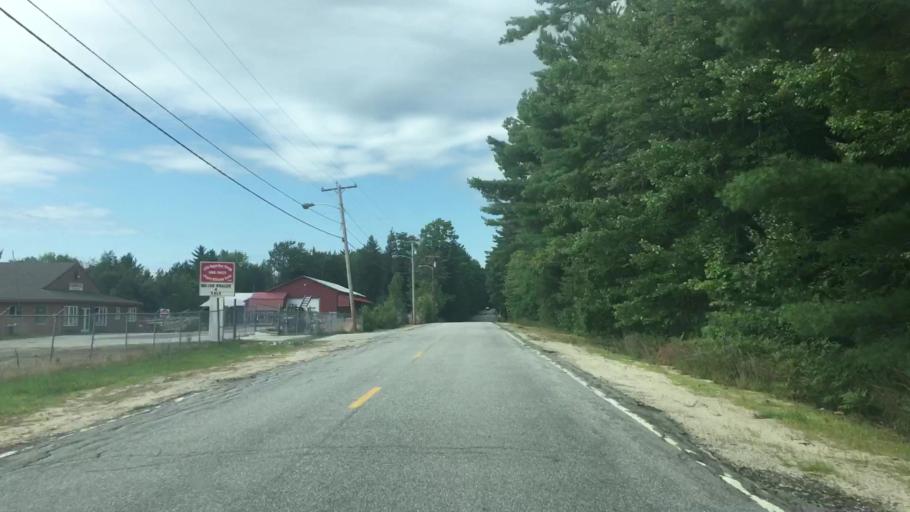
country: US
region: Maine
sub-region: Oxford County
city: Oxford
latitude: 44.0130
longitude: -70.5249
